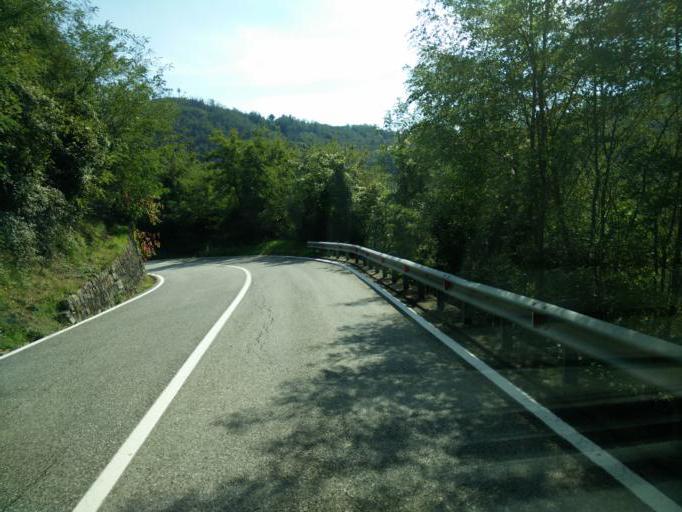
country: IT
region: Liguria
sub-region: Provincia di La Spezia
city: Carrodano
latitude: 44.2421
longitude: 9.6599
